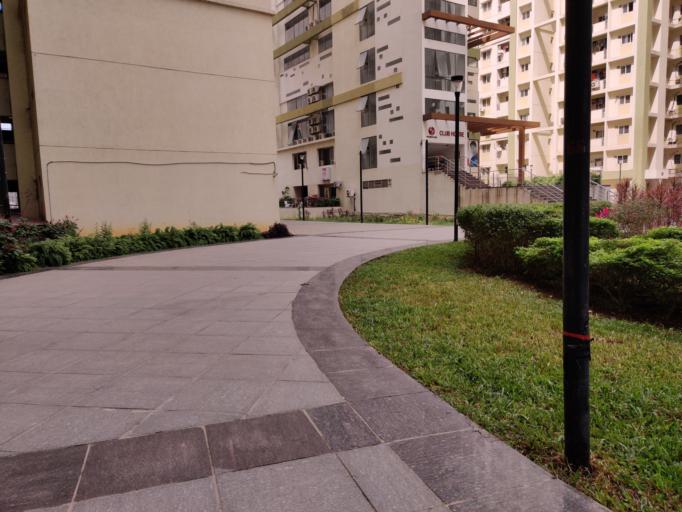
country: IN
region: Telangana
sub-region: Medak
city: Serilingampalle
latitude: 17.4230
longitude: 78.3408
